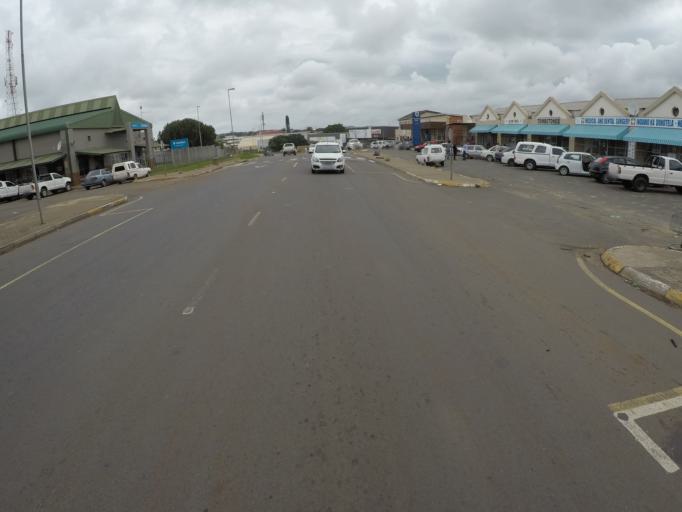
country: ZA
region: KwaZulu-Natal
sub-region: uThungulu District Municipality
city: Empangeni
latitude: -28.7678
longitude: 31.9061
